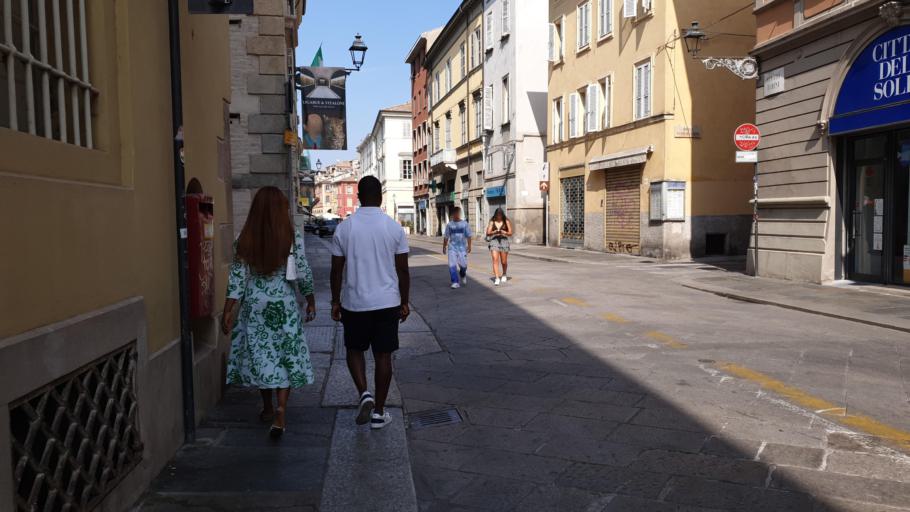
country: IT
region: Emilia-Romagna
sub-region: Provincia di Parma
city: Parma
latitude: 44.7982
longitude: 10.3271
